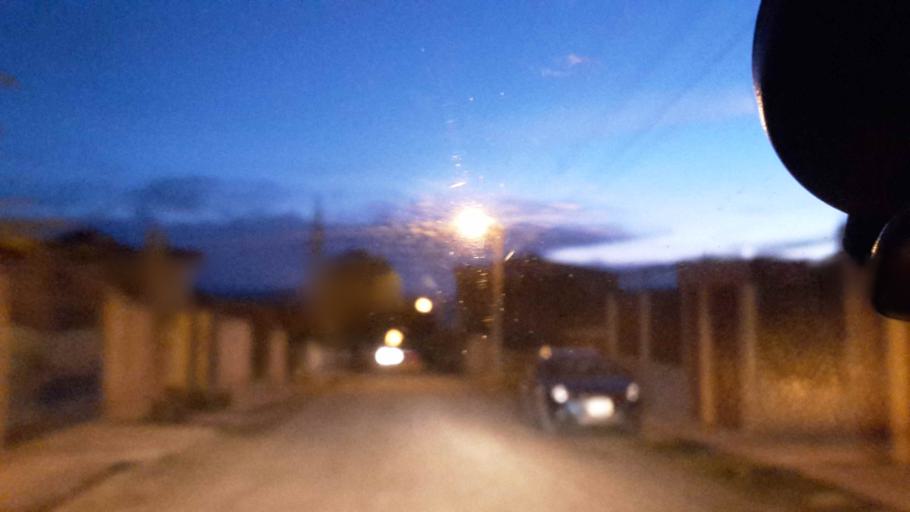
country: BO
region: Cochabamba
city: Cochabamba
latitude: -17.3312
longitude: -66.2177
